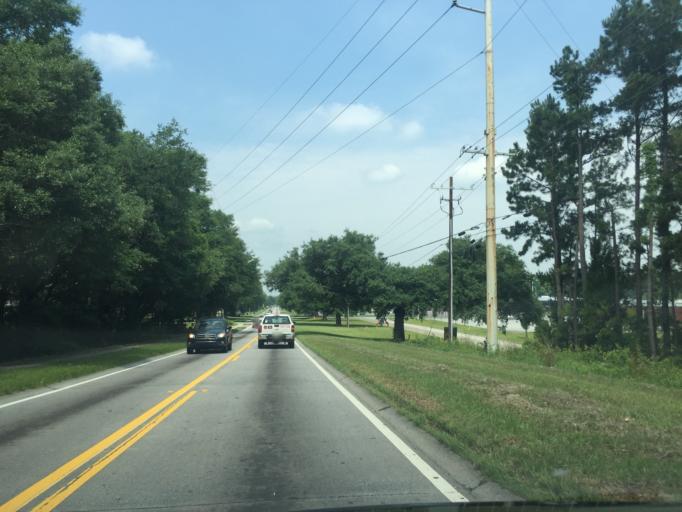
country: US
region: Georgia
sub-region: Chatham County
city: Savannah
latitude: 32.0511
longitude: -81.1275
